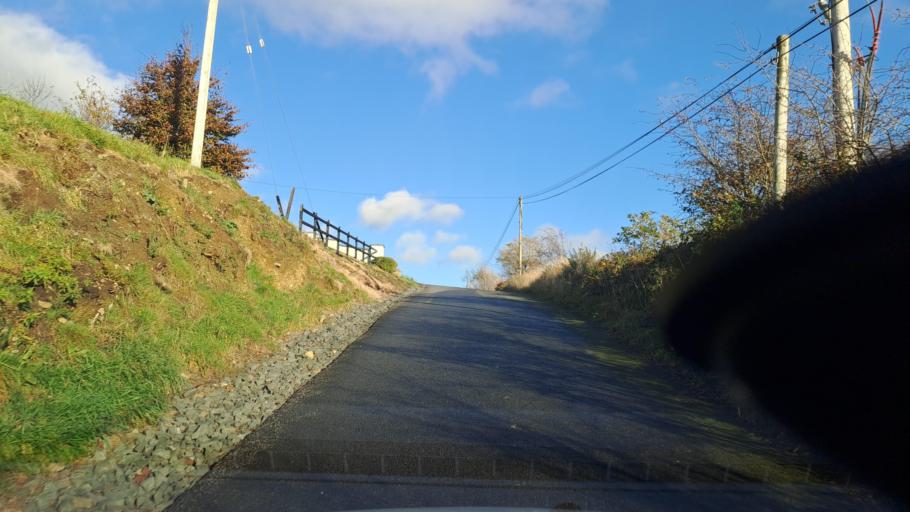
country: IE
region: Ulster
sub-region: An Cabhan
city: Bailieborough
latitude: 53.9198
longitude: -6.9575
